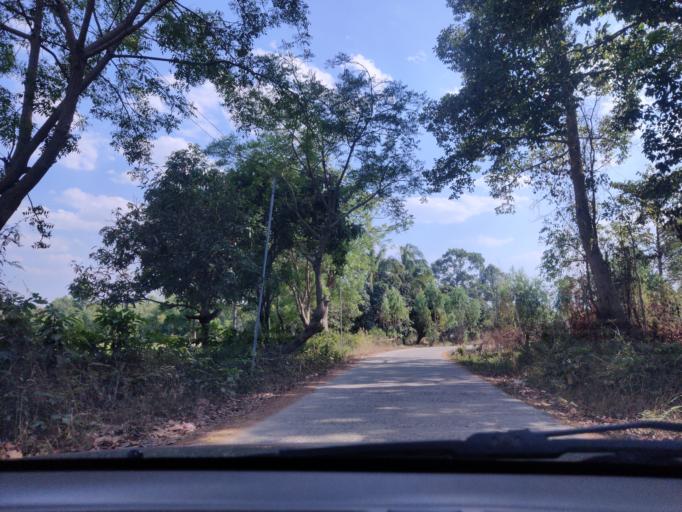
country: TH
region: Sisaket
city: Si Sa Ket
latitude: 15.0722
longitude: 104.3494
